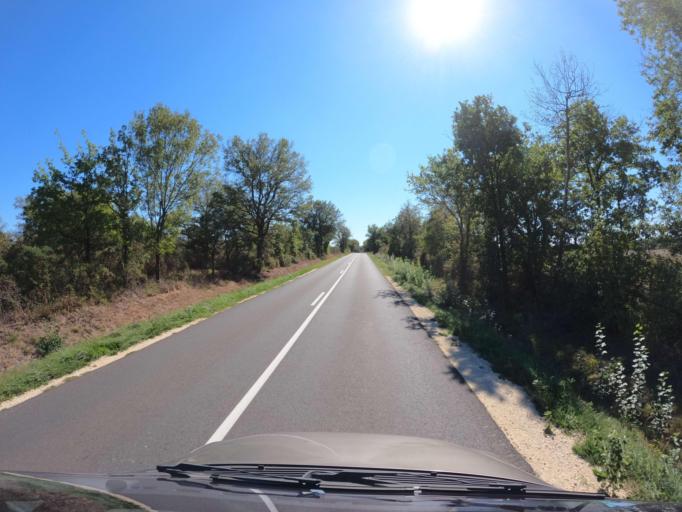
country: FR
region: Poitou-Charentes
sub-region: Departement de la Vienne
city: Lathus-Saint-Remy
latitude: 46.3722
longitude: 0.9316
